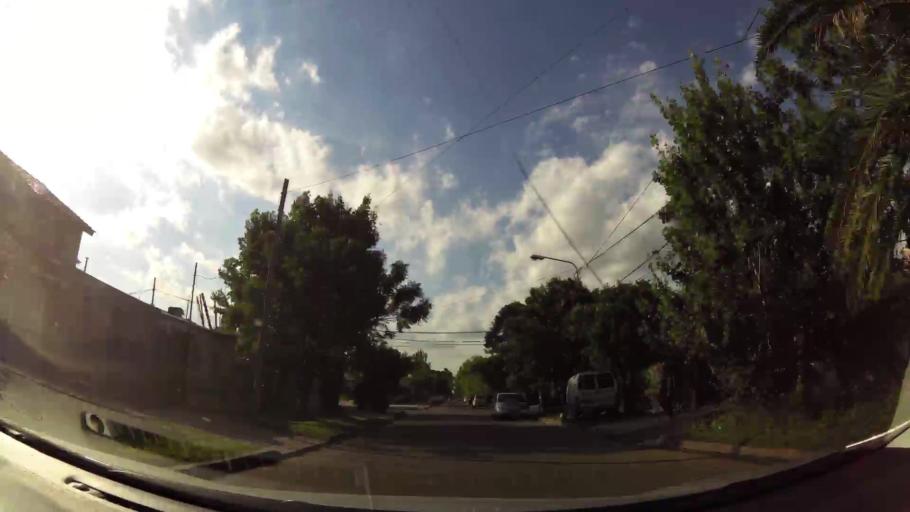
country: AR
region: Buenos Aires
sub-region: Partido de Tigre
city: Tigre
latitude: -34.4718
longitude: -58.6524
